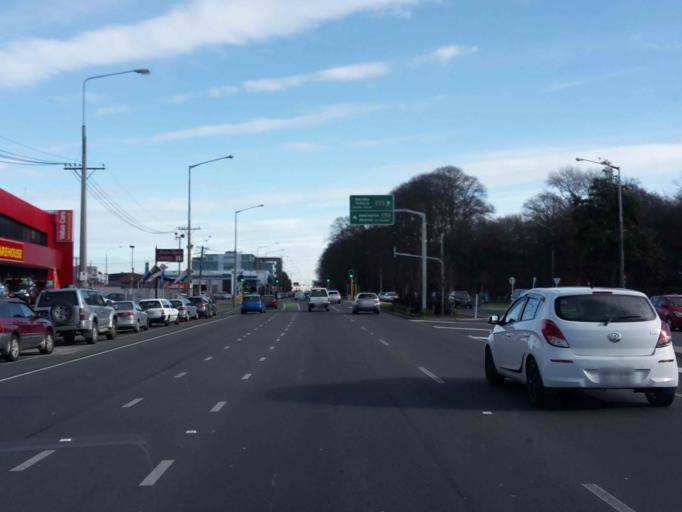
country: NZ
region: Canterbury
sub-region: Christchurch City
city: Christchurch
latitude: -43.5400
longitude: 172.6195
